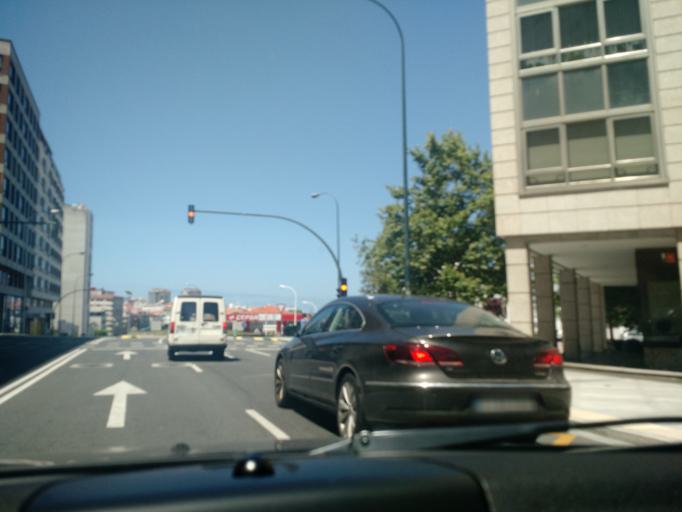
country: ES
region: Galicia
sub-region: Provincia da Coruna
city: A Coruna
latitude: 43.3646
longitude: -8.4183
